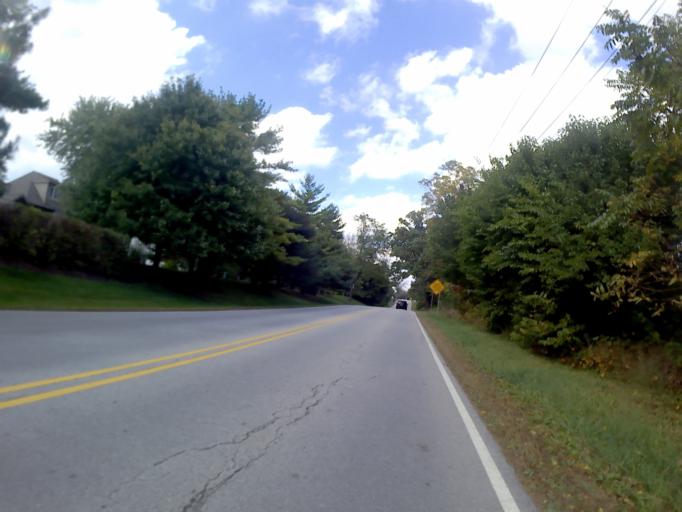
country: US
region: Illinois
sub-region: DuPage County
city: Woodridge
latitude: 41.7540
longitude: -88.0747
